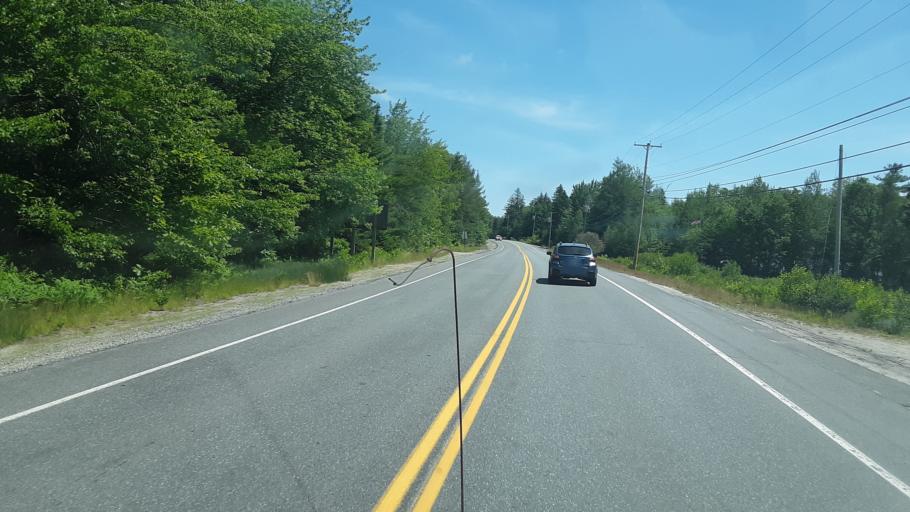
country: US
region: Maine
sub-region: Hancock County
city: Gouldsboro
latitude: 44.4728
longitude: -68.0964
